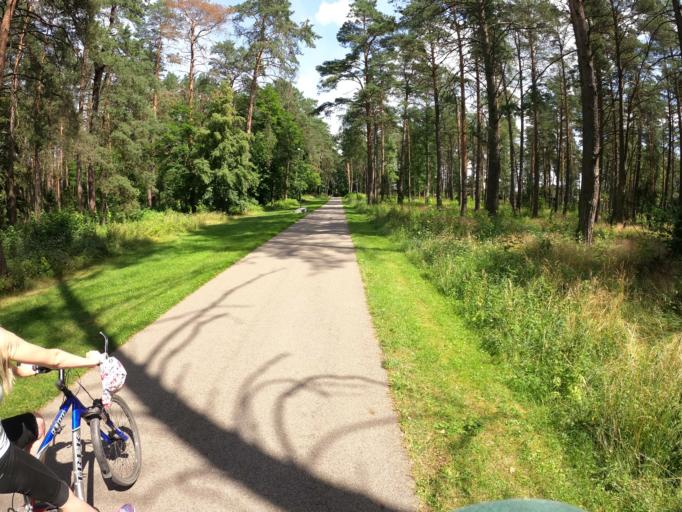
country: LT
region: Alytaus apskritis
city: Druskininkai
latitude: 54.0211
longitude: 23.9977
